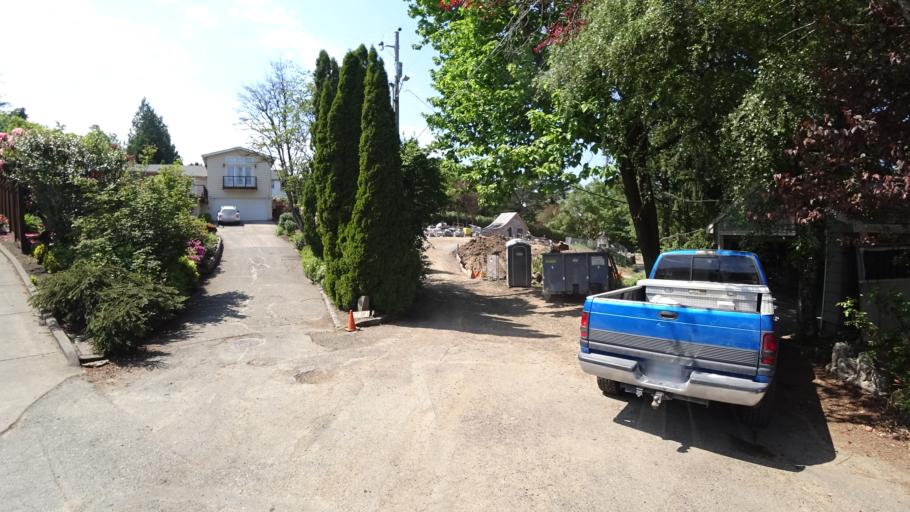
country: US
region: Oregon
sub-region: Multnomah County
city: Portland
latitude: 45.4943
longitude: -122.6995
